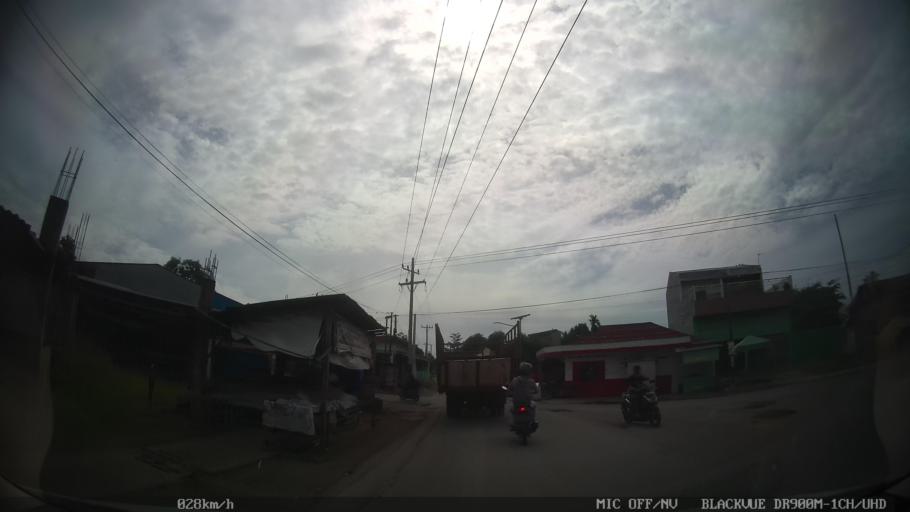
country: ID
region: North Sumatra
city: Percut
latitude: 3.6200
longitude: 98.7659
